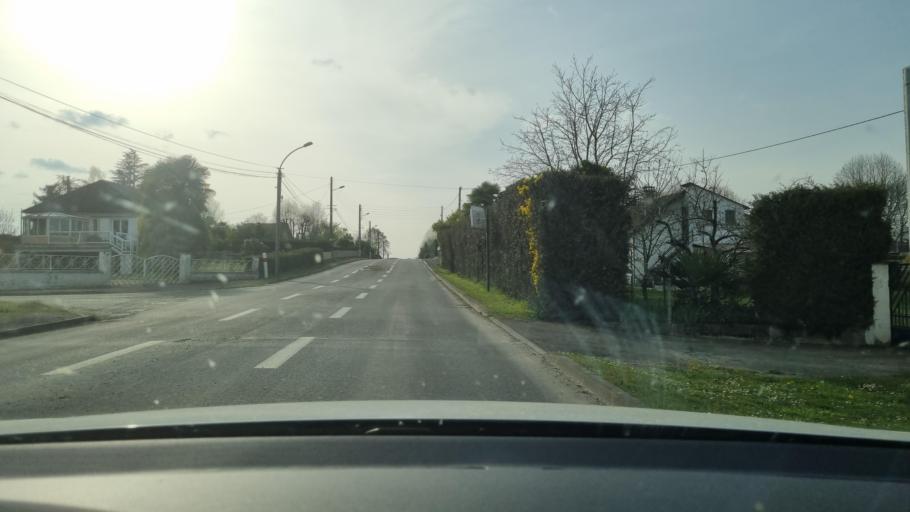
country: FR
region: Aquitaine
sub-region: Departement des Pyrenees-Atlantiques
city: Morlaas
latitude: 43.3585
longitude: -0.2306
